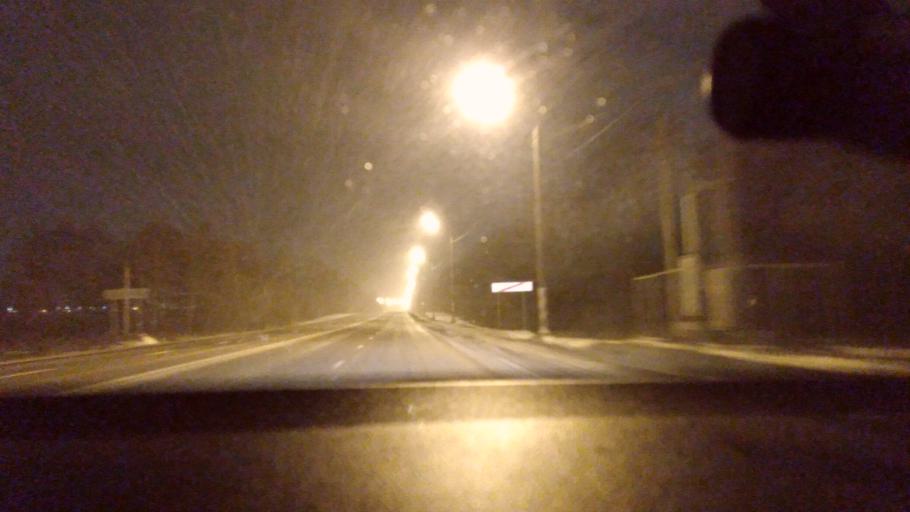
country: RU
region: Moskovskaya
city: Bronnitsy
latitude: 55.4789
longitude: 38.1802
